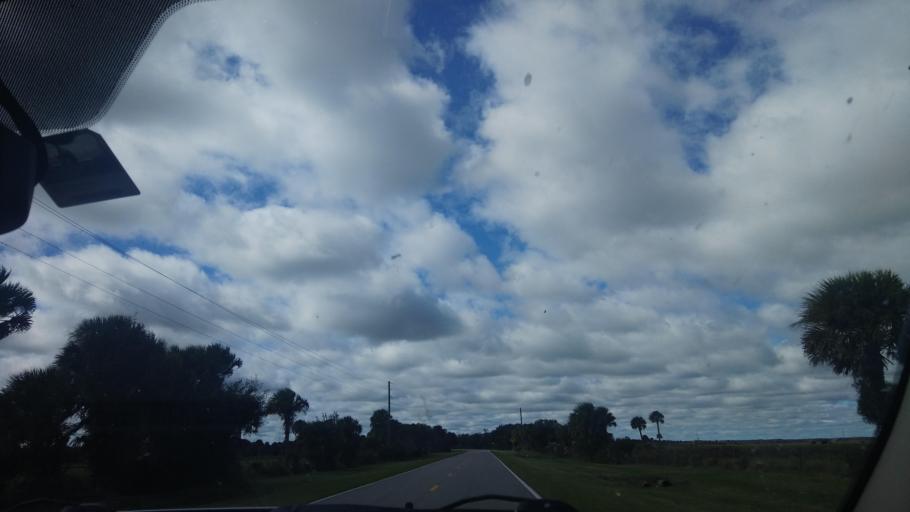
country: US
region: Florida
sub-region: Okeechobee County
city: Okeechobee
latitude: 27.3949
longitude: -80.9090
